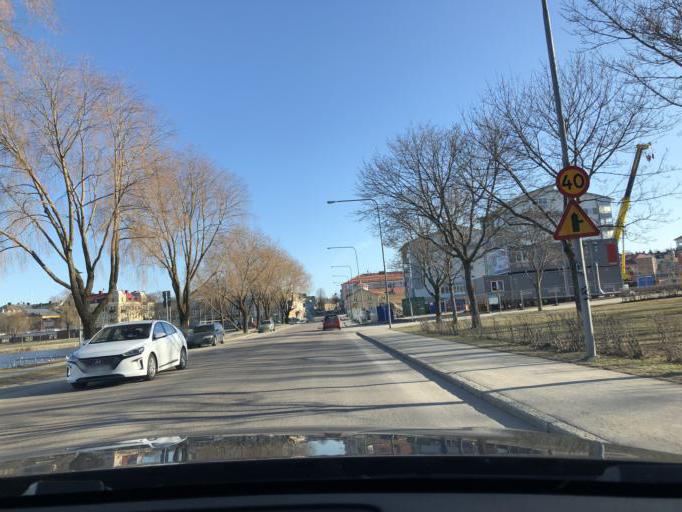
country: SE
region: Gaevleborg
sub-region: Hudiksvalls Kommun
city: Hudiksvall
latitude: 61.7309
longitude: 17.1048
